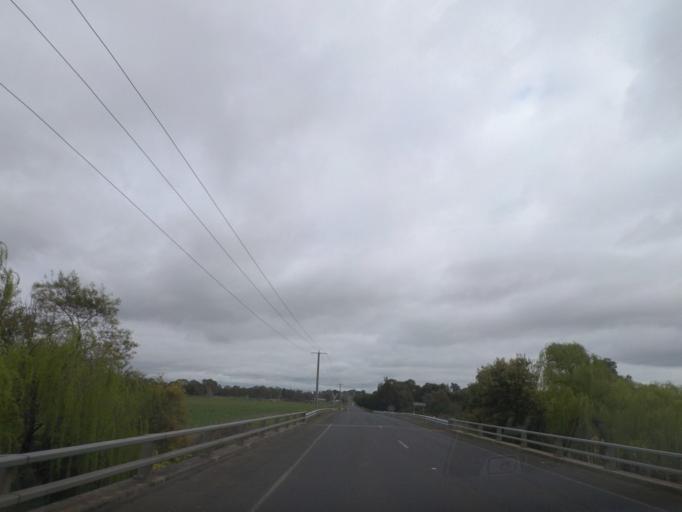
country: AU
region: Victoria
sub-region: Whittlesea
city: Mernda
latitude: -37.5705
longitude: 145.1189
